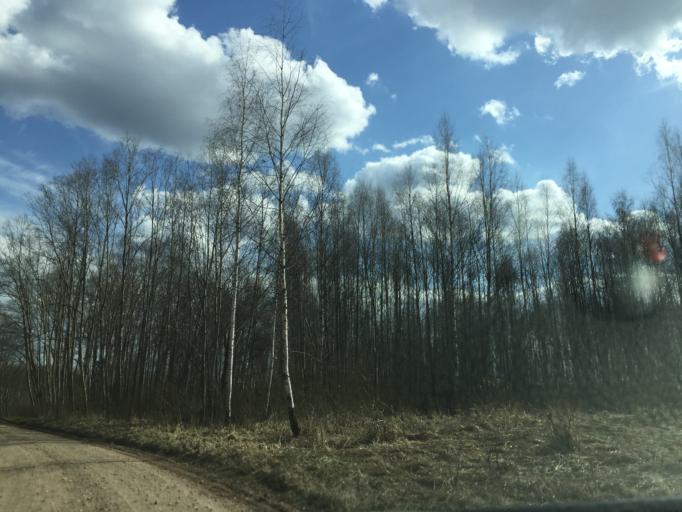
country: LV
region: Skriveri
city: Skriveri
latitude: 56.8000
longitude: 25.1611
